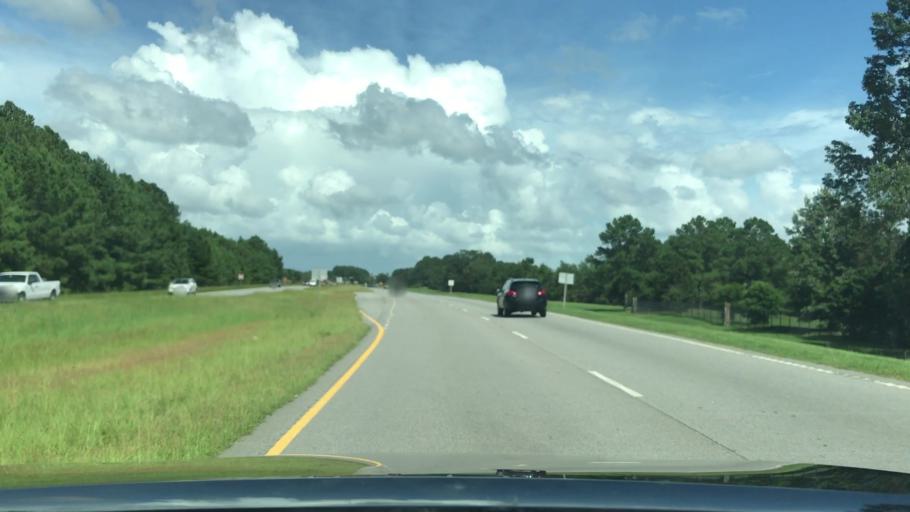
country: US
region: South Carolina
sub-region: Jasper County
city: Hardeeville
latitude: 32.3014
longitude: -80.9642
